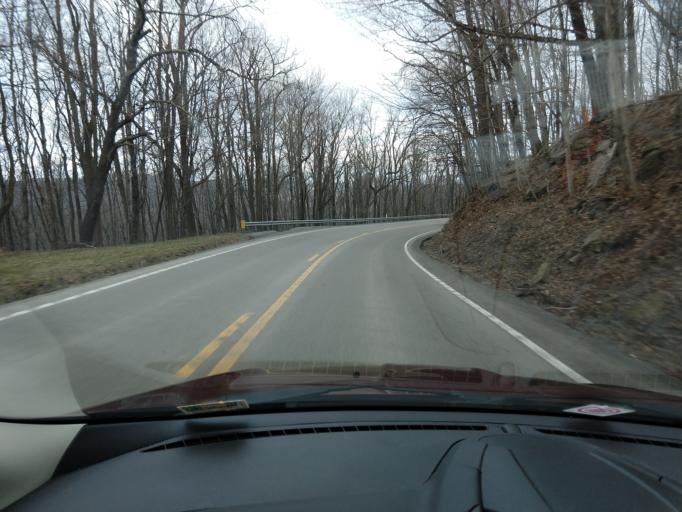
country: US
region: West Virginia
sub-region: Randolph County
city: Elkins
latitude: 38.6520
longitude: -79.9230
